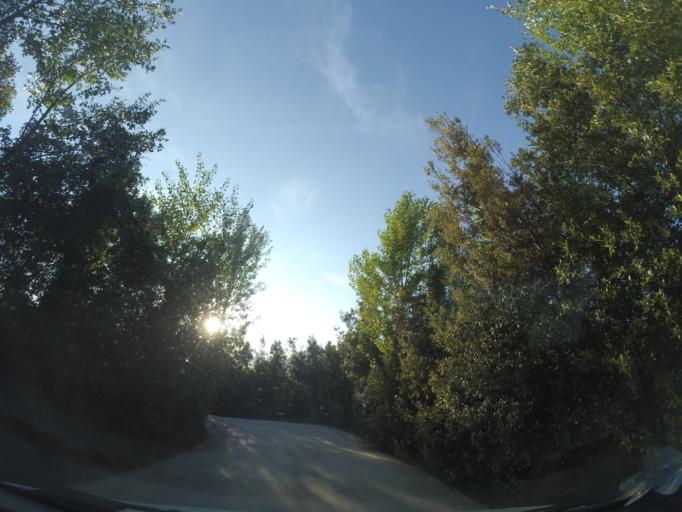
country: IT
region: Tuscany
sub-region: Province of Arezzo
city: Castiglion Fibocchi
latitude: 43.5298
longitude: 11.7769
